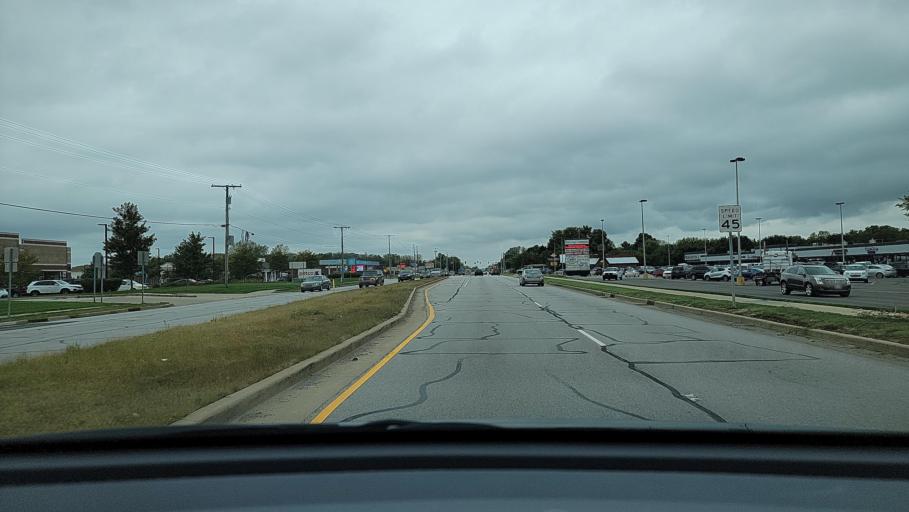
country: US
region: Indiana
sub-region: Porter County
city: Portage
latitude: 41.5506
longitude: -87.1842
